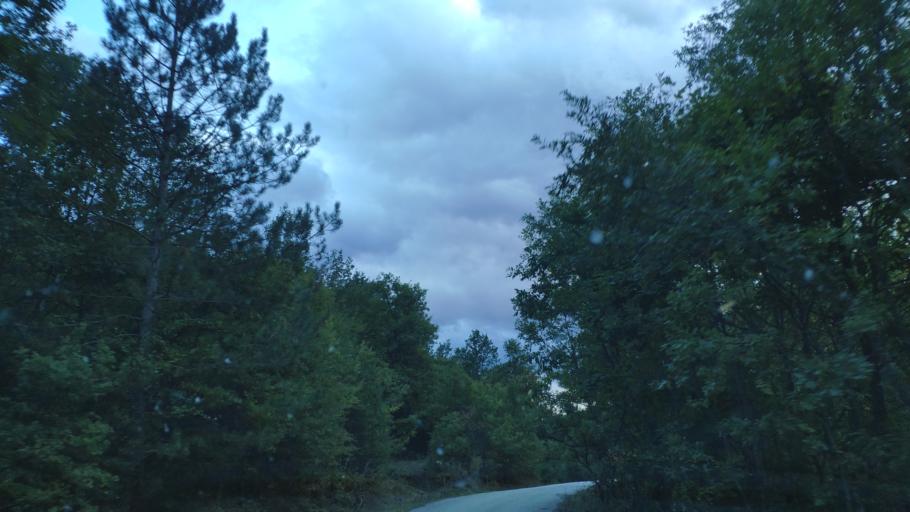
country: AL
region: Korce
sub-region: Rrethi i Kolonjes
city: Erseke
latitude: 40.2604
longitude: 20.8582
